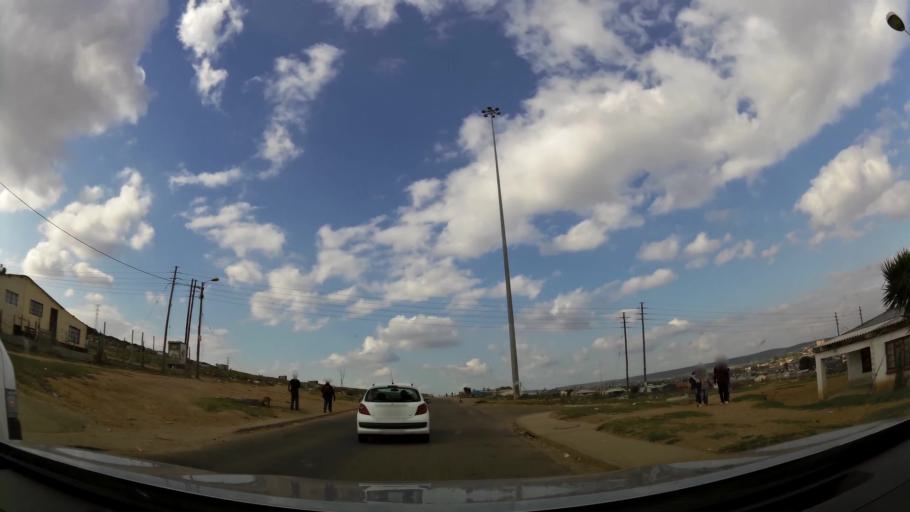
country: ZA
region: Eastern Cape
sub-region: Nelson Mandela Bay Metropolitan Municipality
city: Uitenhage
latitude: -33.7308
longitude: 25.3881
